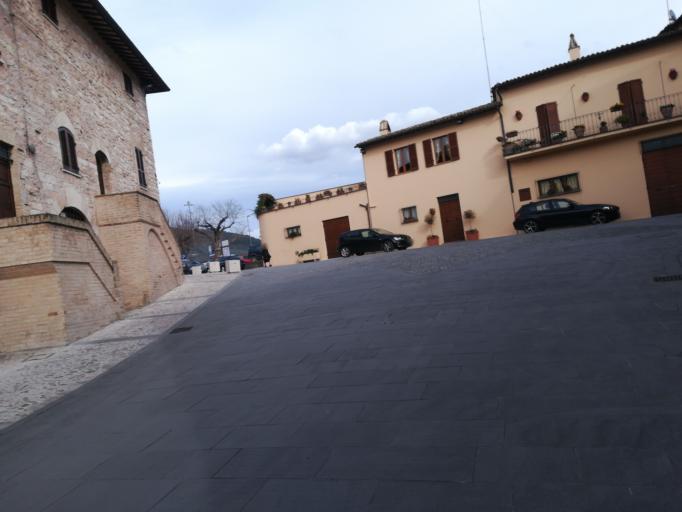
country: IT
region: Umbria
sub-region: Provincia di Perugia
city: Spello
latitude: 42.9958
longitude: 12.6713
